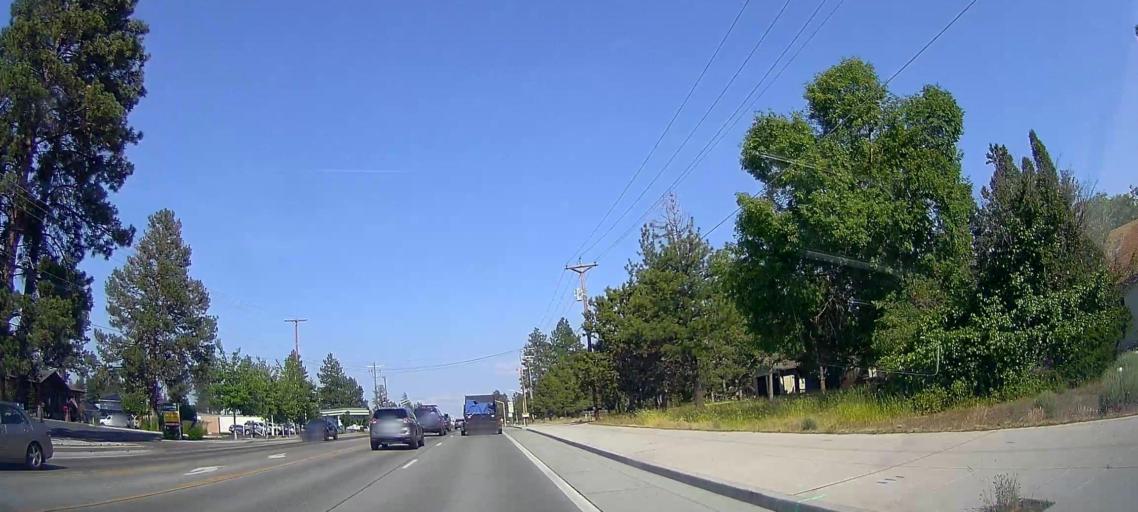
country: US
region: Oregon
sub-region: Deschutes County
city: Bend
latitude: 44.0369
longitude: -121.2864
